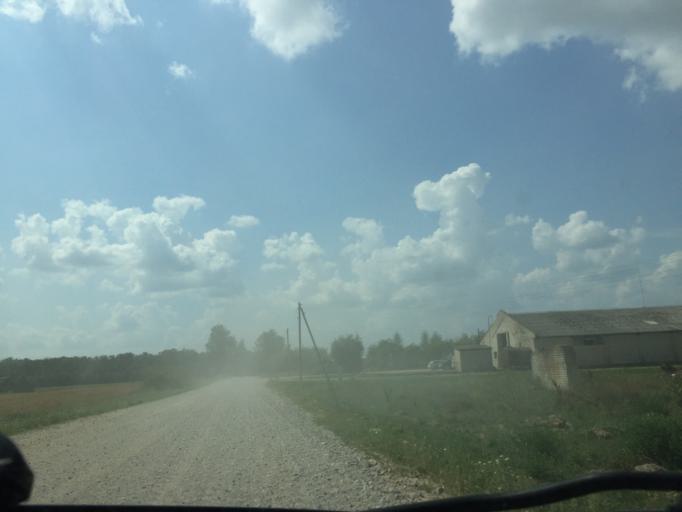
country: LT
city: Zagare
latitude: 56.4020
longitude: 23.2377
